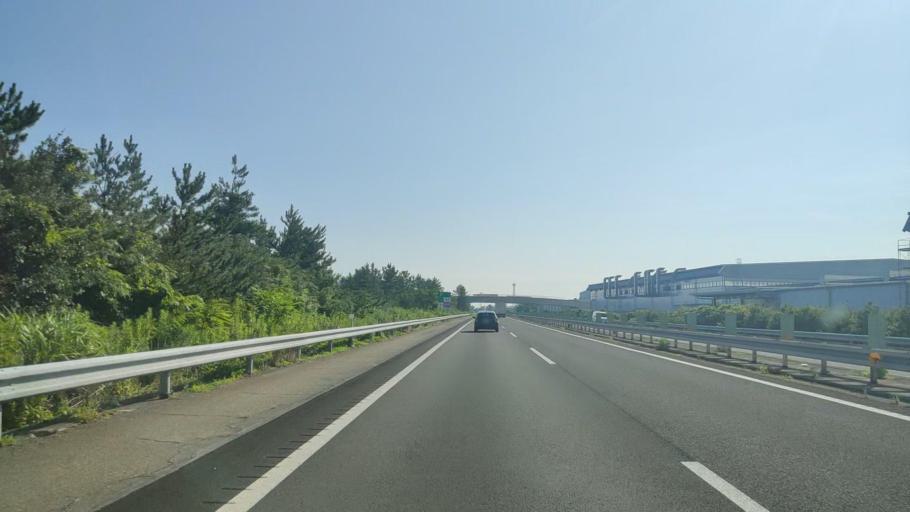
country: JP
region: Ishikawa
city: Komatsu
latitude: 36.3887
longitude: 136.3822
